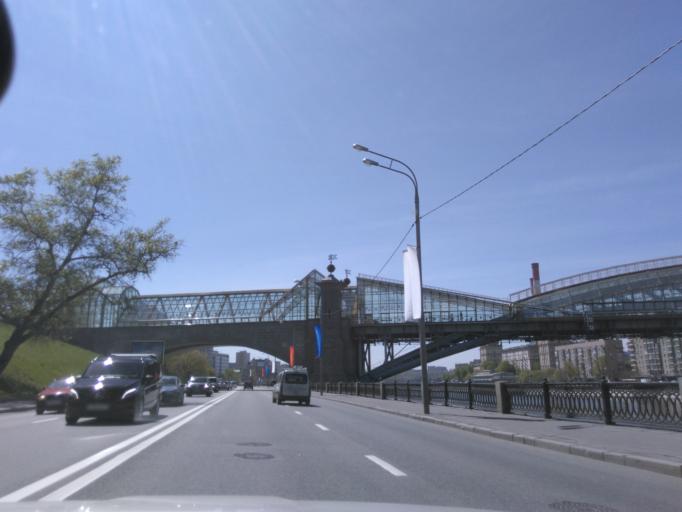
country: RU
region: Moskovskaya
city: Dorogomilovo
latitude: 55.7417
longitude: 37.5726
